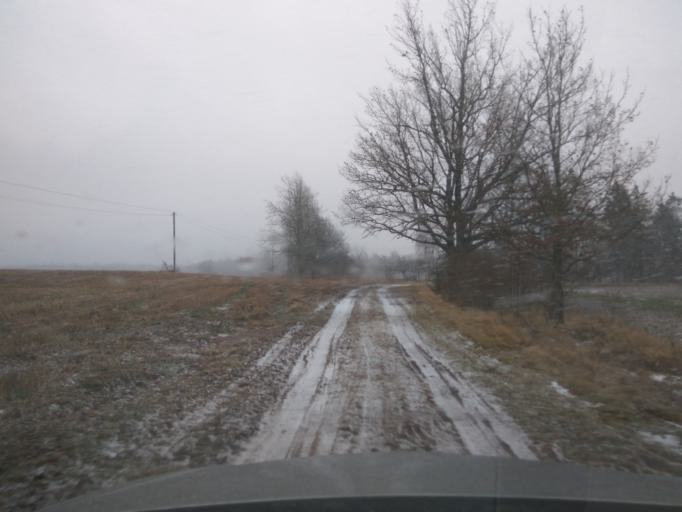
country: LV
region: Saldus Rajons
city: Saldus
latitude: 56.8435
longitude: 22.3803
